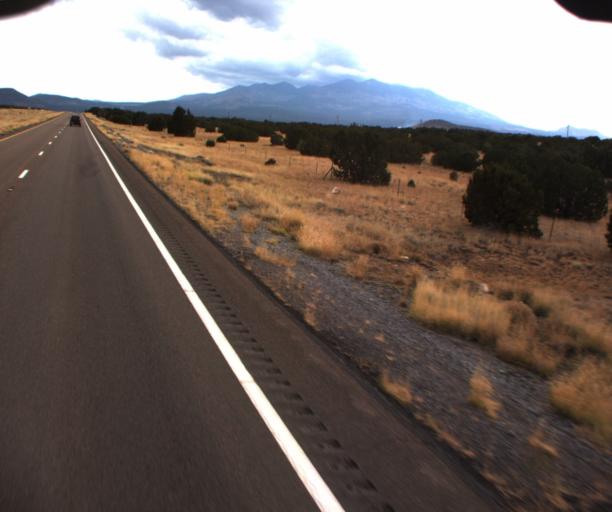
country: US
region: Arizona
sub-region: Coconino County
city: Flagstaff
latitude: 35.4831
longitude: -111.5564
